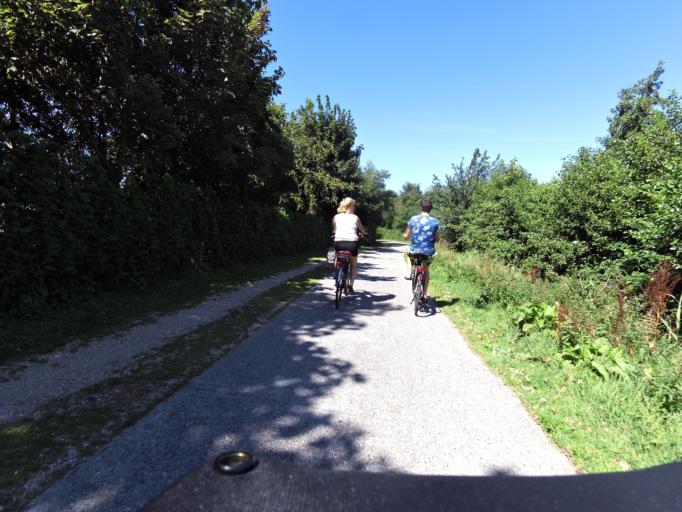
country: NL
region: Zeeland
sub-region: Schouwen-Duiveland
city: Haamstede
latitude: 51.7195
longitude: 3.7273
